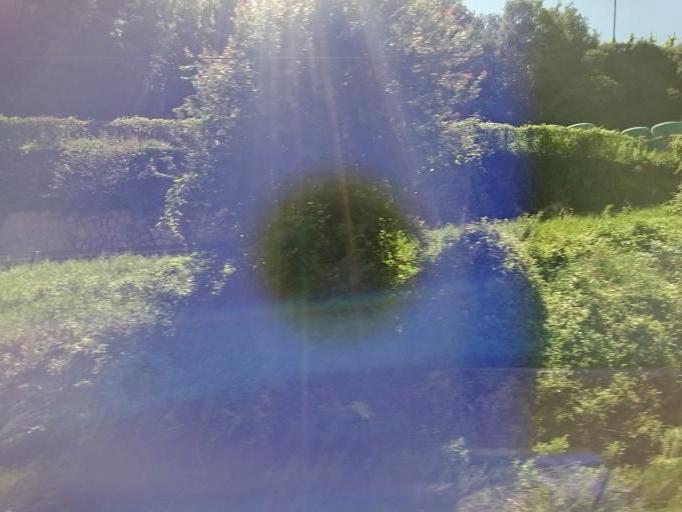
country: IT
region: Trentino-Alto Adige
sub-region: Bolzano
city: Velturno
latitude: 46.6506
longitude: 11.5883
